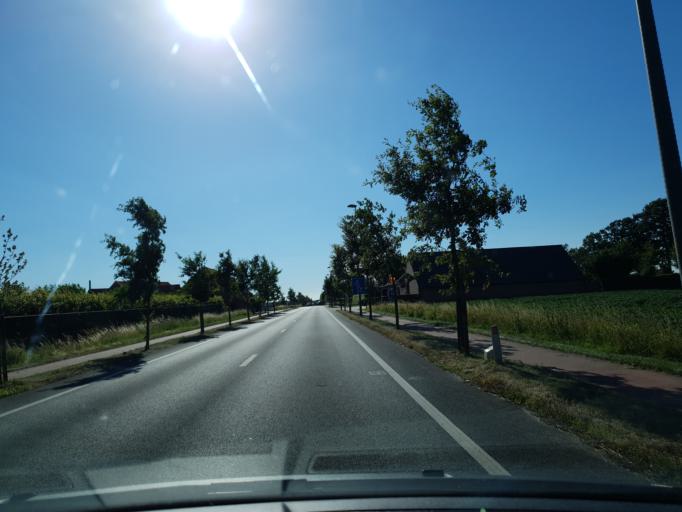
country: BE
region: Flanders
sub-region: Provincie Antwerpen
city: Brecht
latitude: 51.4042
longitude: 4.6706
